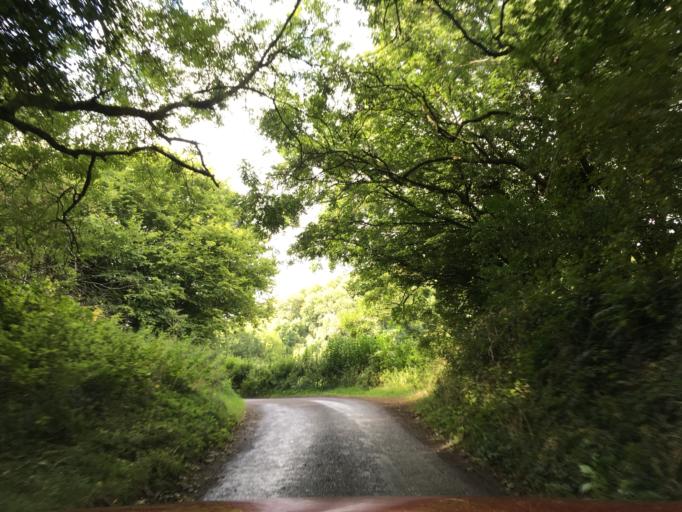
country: GB
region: England
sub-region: South Gloucestershire
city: Falfield
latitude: 51.6118
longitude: -2.4556
